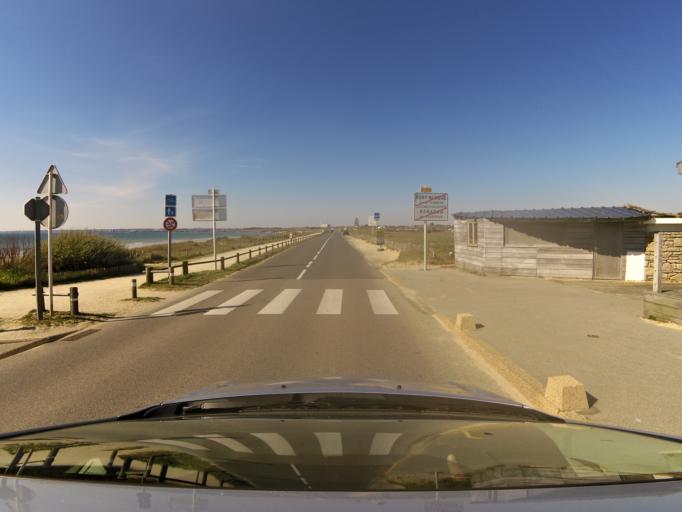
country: FR
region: Brittany
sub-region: Departement du Morbihan
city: Guidel-Plage
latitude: 47.7379
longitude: -3.5014
